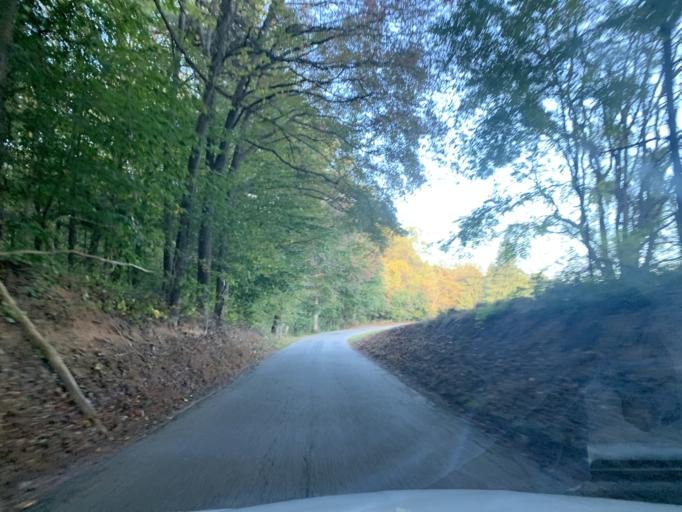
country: US
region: Maryland
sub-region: Harford County
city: Fallston
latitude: 39.4990
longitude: -76.4447
